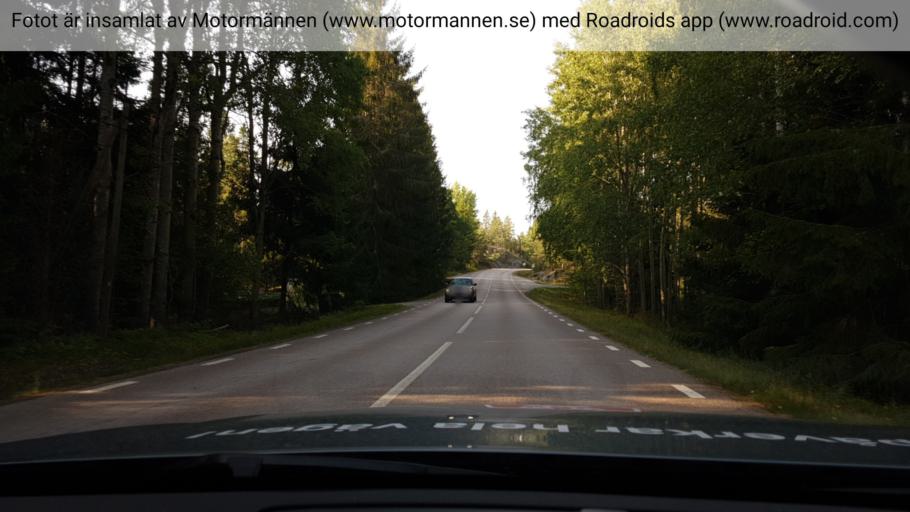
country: SE
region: Soedermanland
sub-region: Strangnas Kommun
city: Mariefred
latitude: 59.1785
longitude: 17.1891
